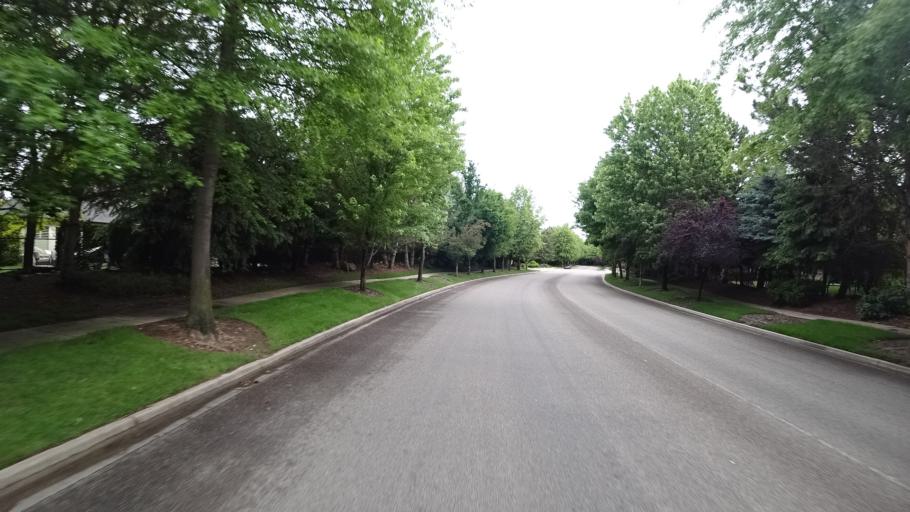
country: US
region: Idaho
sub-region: Ada County
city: Eagle
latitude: 43.6833
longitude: -116.3590
